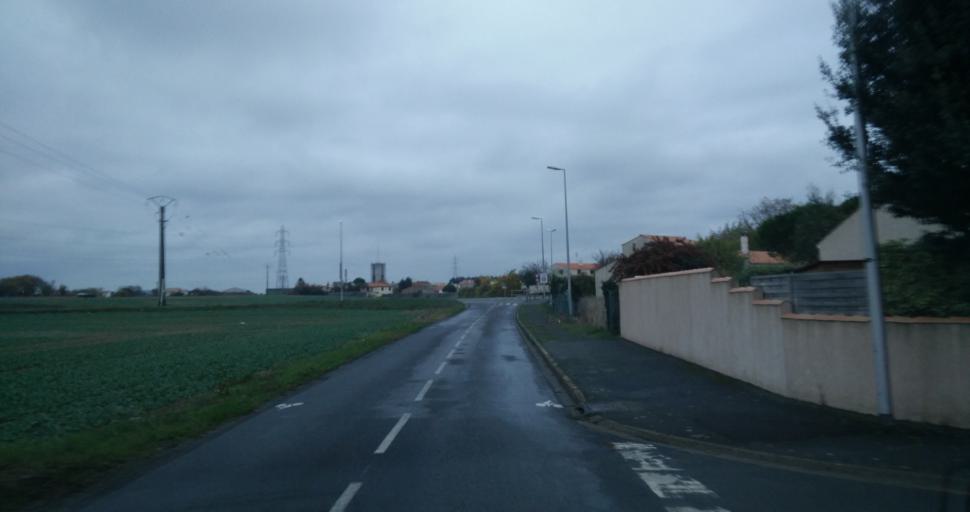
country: FR
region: Poitou-Charentes
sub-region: Departement de la Charente-Maritime
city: Puilboreau
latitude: 46.1880
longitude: -1.1226
